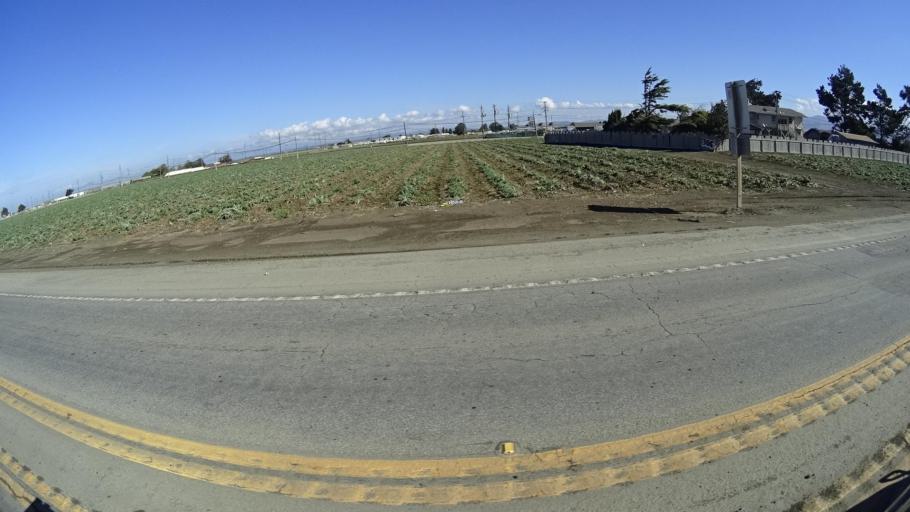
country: US
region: California
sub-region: Monterey County
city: Boronda
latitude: 36.6848
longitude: -121.6790
